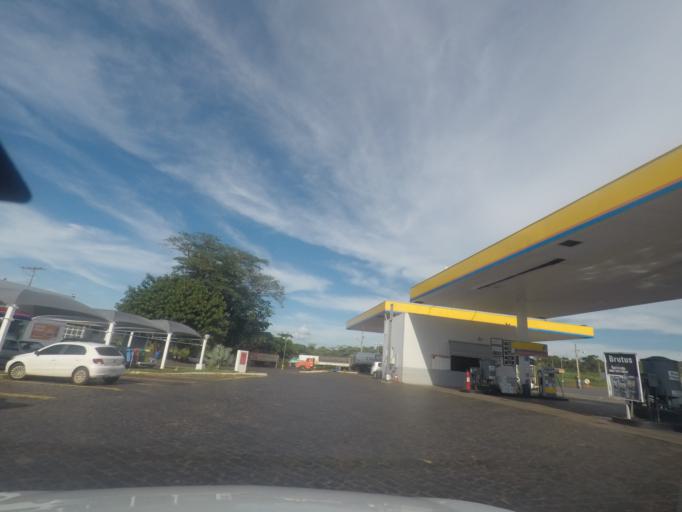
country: BR
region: Minas Gerais
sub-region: Monte Alegre De Minas
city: Monte Alegre de Minas
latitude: -18.8781
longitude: -49.0558
